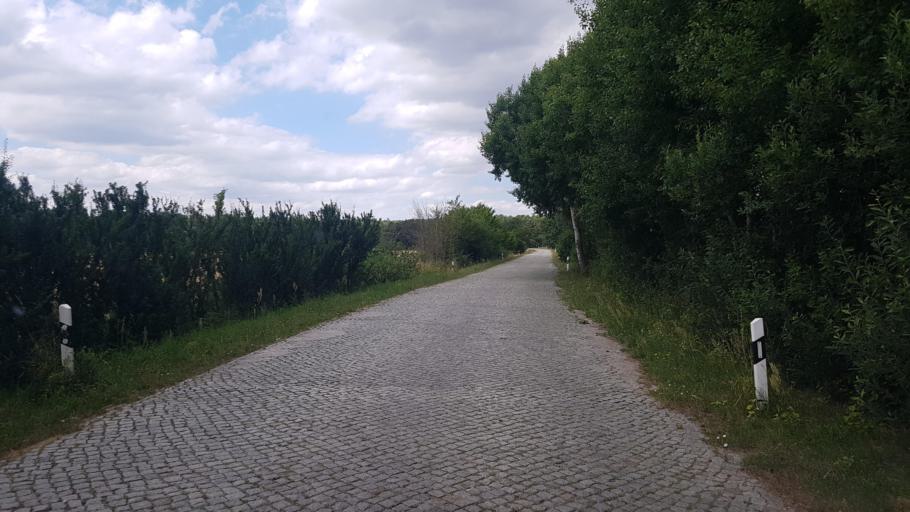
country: DE
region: Brandenburg
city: Juterbog
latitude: 52.0399
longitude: 13.1242
